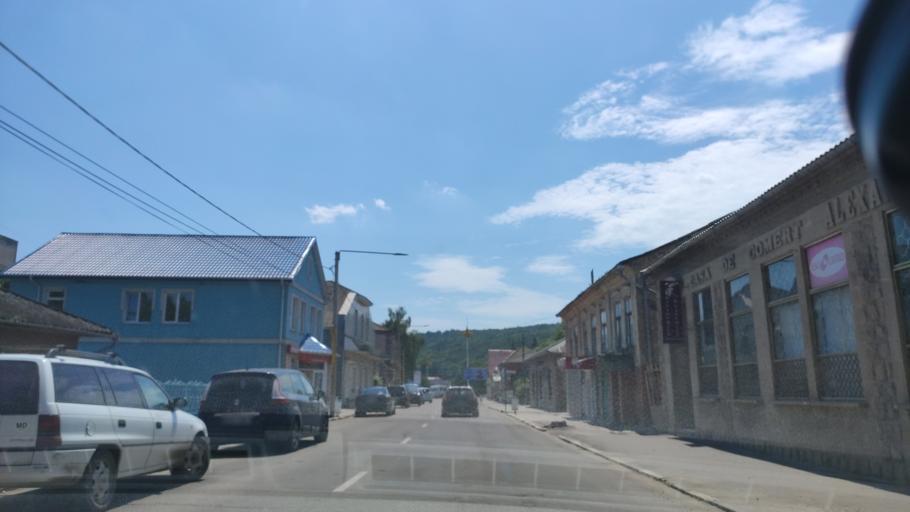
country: MD
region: Raionul Soroca
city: Soroca
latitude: 48.1588
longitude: 28.2999
